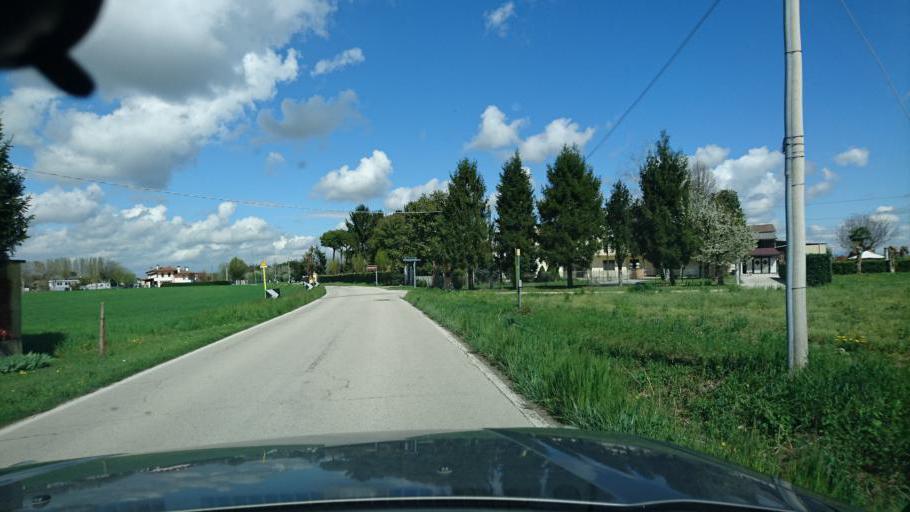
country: IT
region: Veneto
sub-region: Provincia di Padova
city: Santa Maria di Non
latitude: 45.5047
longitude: 11.8511
